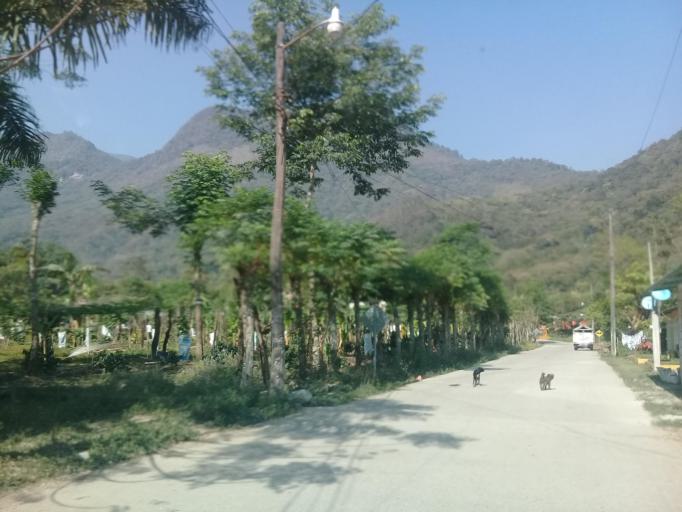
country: MX
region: Veracruz
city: Rafael Delgado
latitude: 18.7822
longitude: -97.0158
